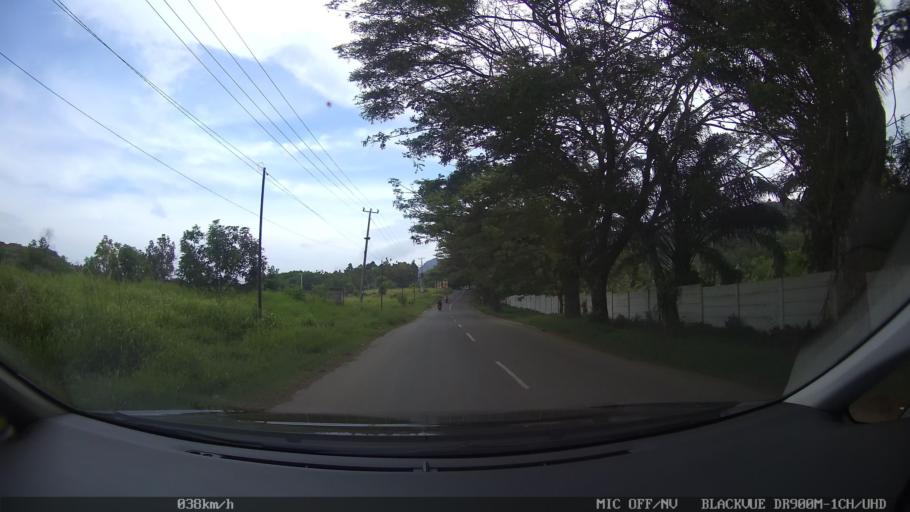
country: ID
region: Lampung
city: Bandarlampung
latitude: -5.4086
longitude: 105.1945
